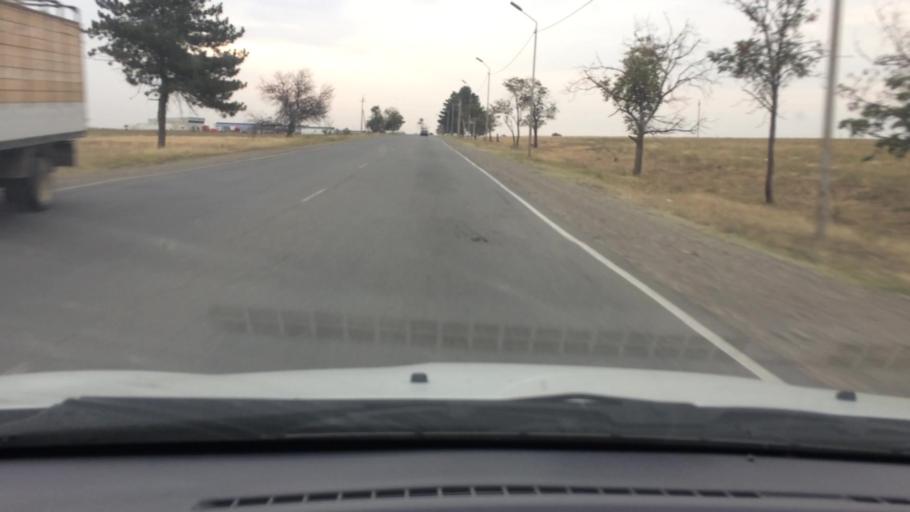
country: GE
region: Kvemo Kartli
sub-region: Marneuli
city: Marneuli
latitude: 41.5156
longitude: 44.7857
